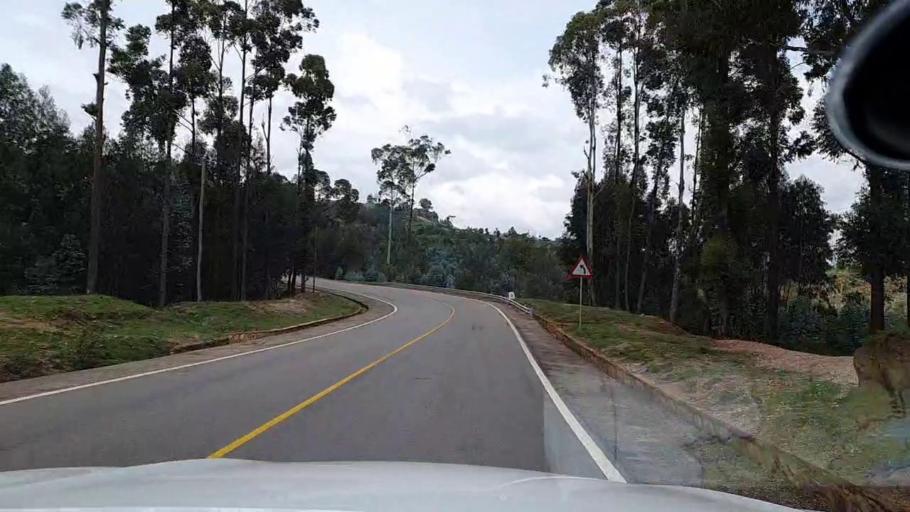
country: RW
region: Southern Province
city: Nzega
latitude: -2.5051
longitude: 29.5052
